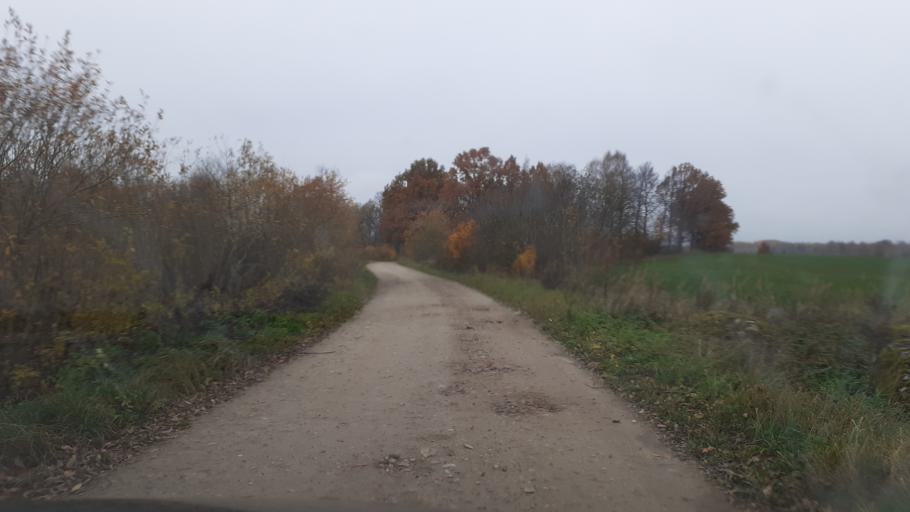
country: LV
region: Saldus Rajons
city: Saldus
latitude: 56.8689
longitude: 22.3398
